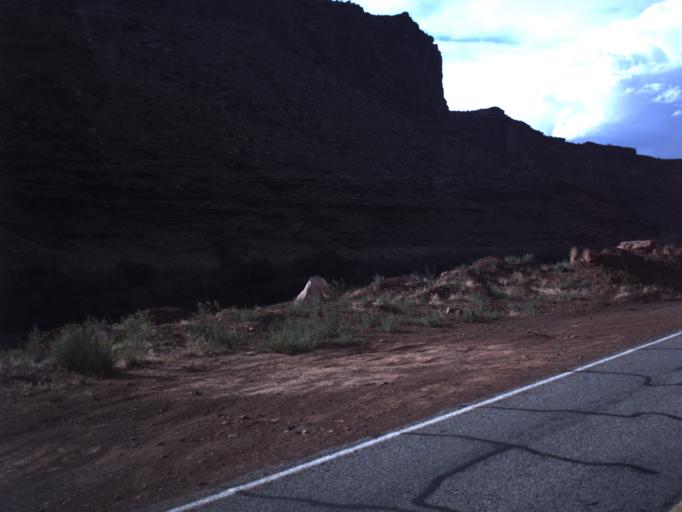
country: US
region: Utah
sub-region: Grand County
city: Moab
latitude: 38.7823
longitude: -109.3322
